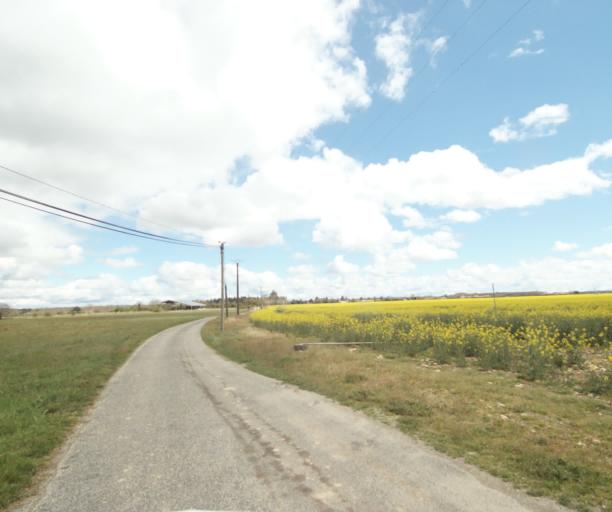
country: FR
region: Midi-Pyrenees
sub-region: Departement de l'Ariege
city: Saverdun
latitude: 43.2452
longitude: 1.5998
